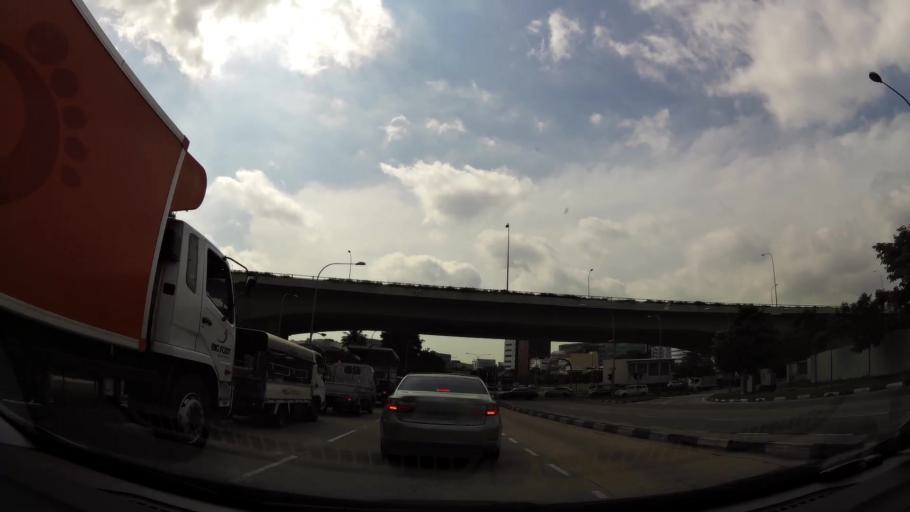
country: SG
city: Singapore
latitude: 1.3438
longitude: 103.8913
